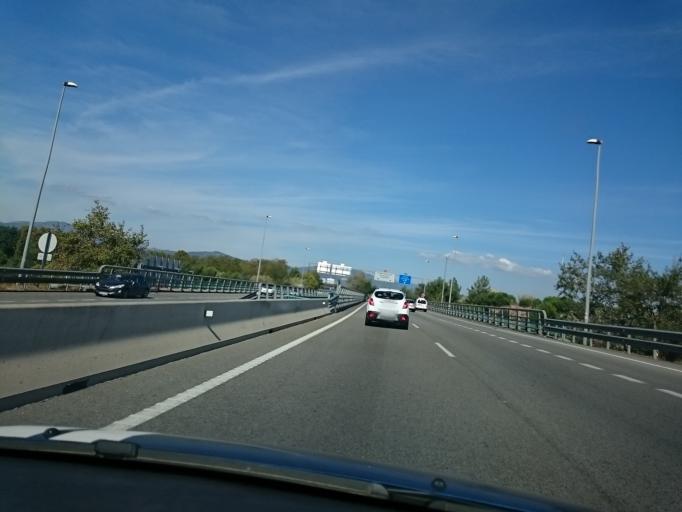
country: ES
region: Catalonia
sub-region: Provincia de Barcelona
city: Santa Perpetua de Mogoda
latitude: 41.5424
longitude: 2.1891
